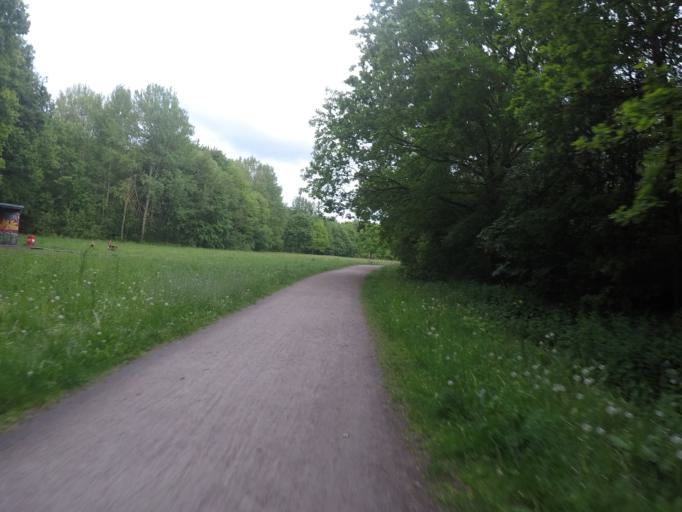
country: DE
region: Schleswig-Holstein
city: Bonningstedt
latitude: 53.6472
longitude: 9.9470
